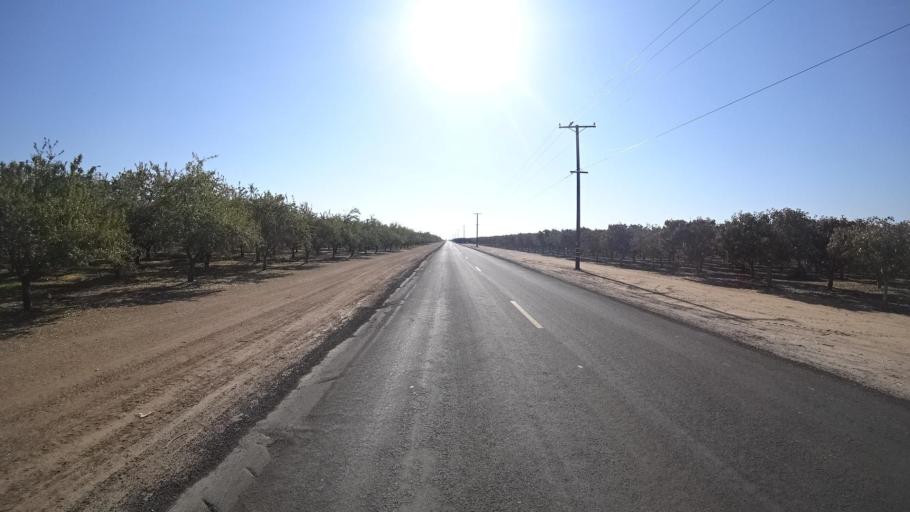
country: US
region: California
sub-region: Tulare County
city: Richgrove
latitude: 35.7392
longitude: -119.1343
